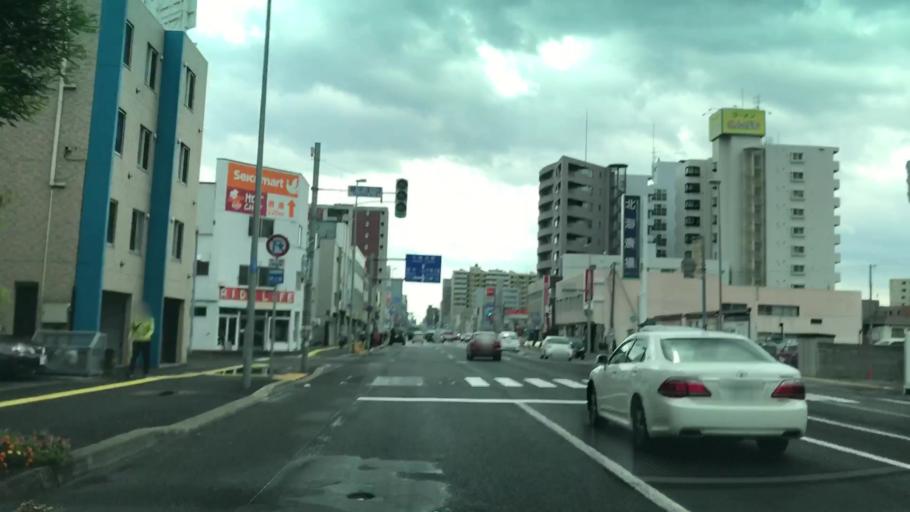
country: JP
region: Hokkaido
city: Sapporo
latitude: 43.0527
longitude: 141.3694
